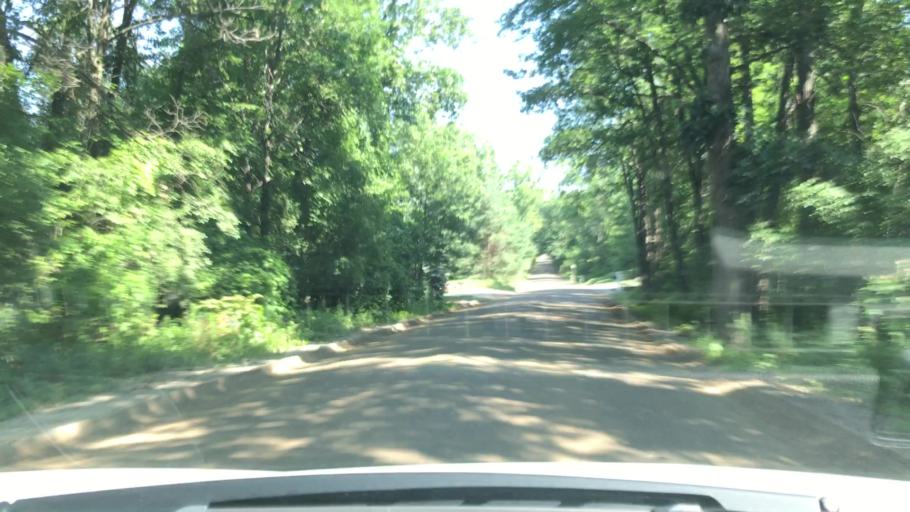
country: US
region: Michigan
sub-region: Oakland County
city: Clarkston
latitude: 42.7800
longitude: -83.3421
